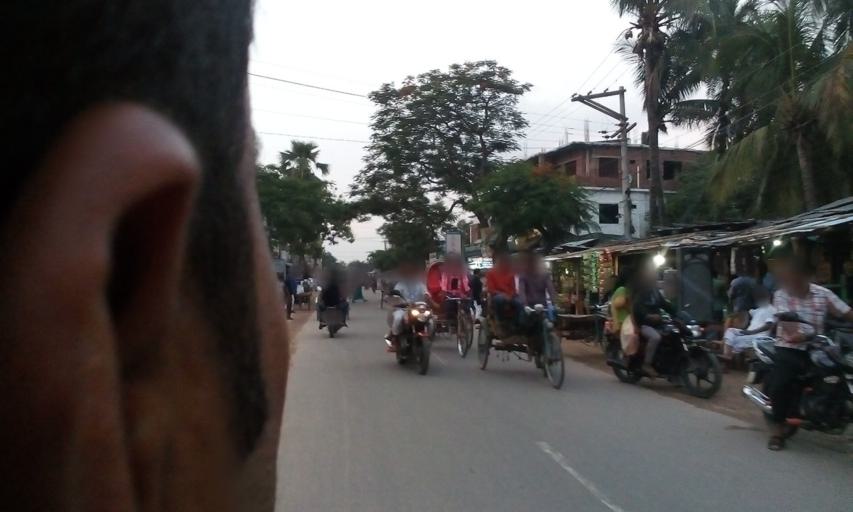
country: IN
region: West Bengal
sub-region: Dakshin Dinajpur
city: Balurghat
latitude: 25.3878
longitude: 88.9888
